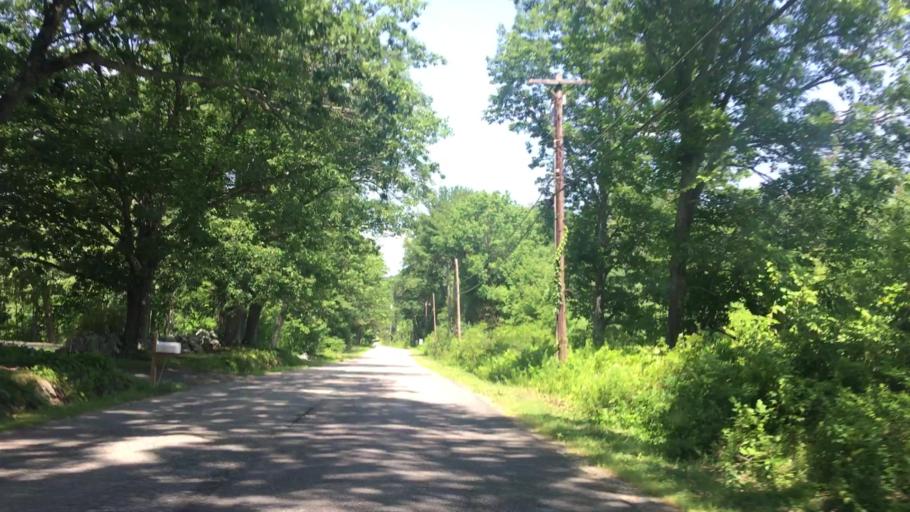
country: US
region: Maine
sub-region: Kennebec County
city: Wayne
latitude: 44.3412
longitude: -70.0606
